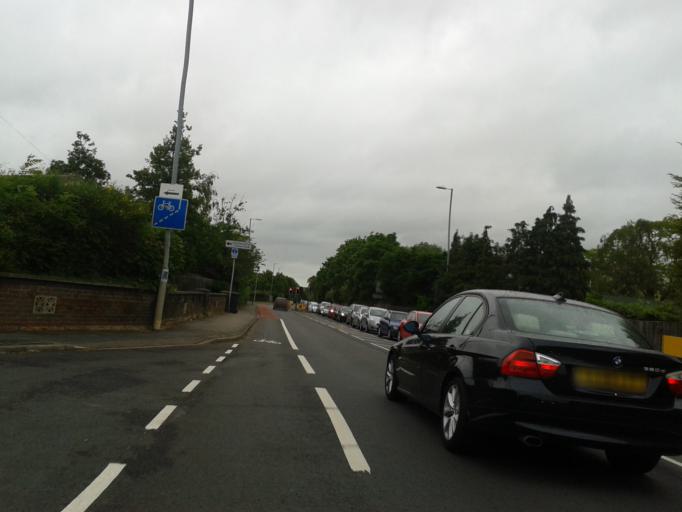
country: GB
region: England
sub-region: Cambridgeshire
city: Histon
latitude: 52.2442
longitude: 0.1114
